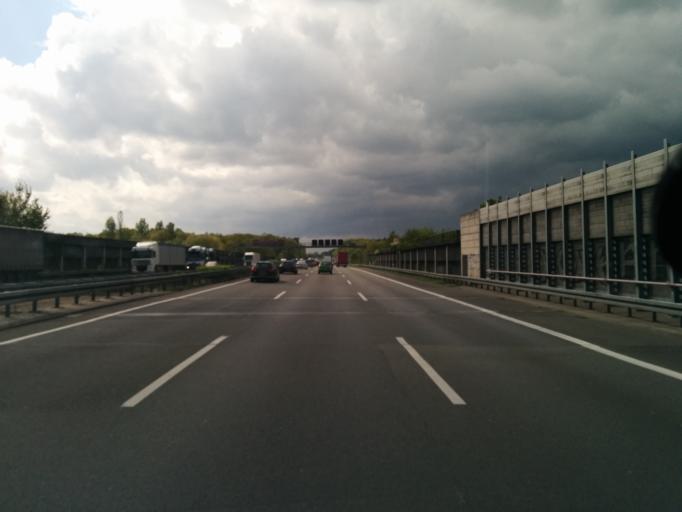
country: DE
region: Lower Saxony
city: Braunschweig
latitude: 52.3116
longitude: 10.5883
